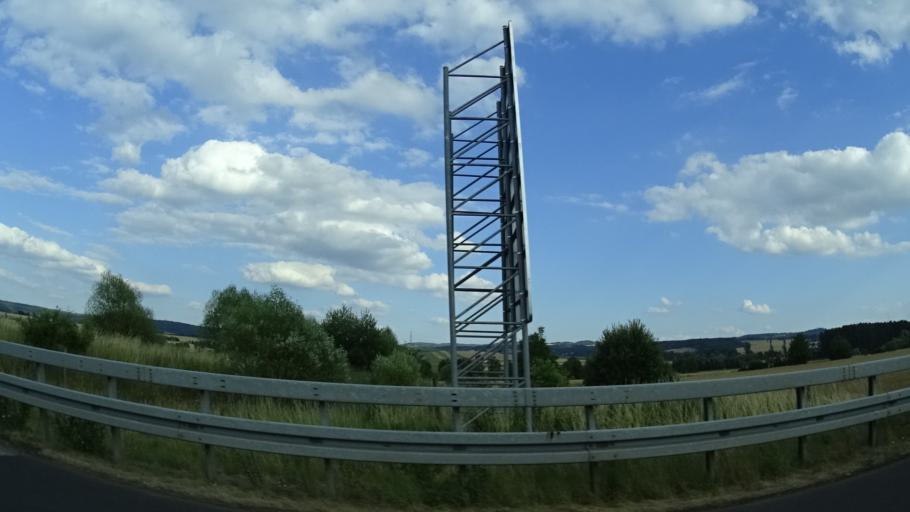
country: DE
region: Hesse
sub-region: Regierungsbezirk Kassel
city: Neuhof
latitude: 50.4387
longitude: 9.5997
